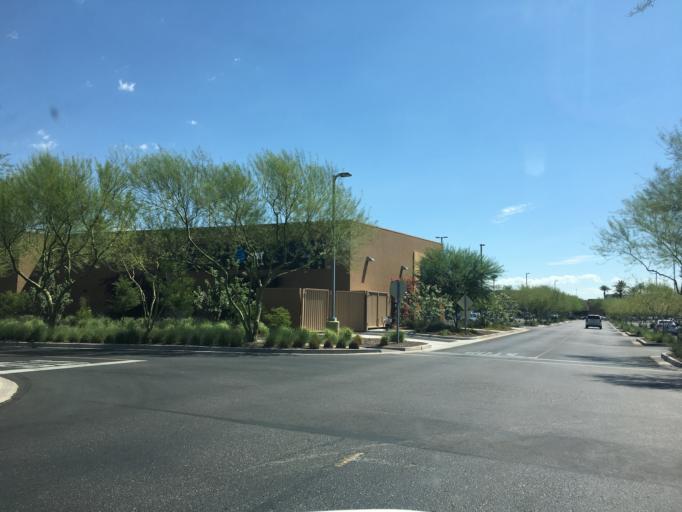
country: US
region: Arizona
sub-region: Maricopa County
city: Tempe
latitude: 33.4317
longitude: -111.9050
